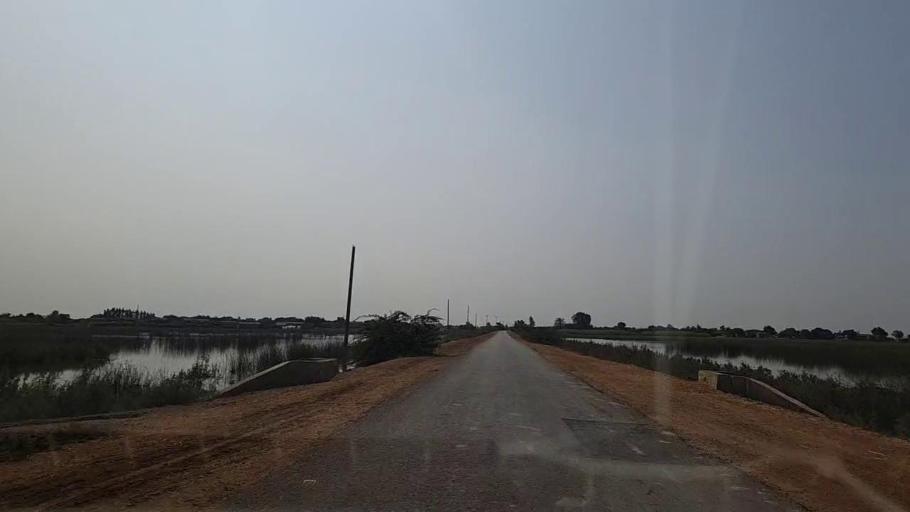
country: PK
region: Sindh
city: Chuhar Jamali
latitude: 24.3088
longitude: 67.9380
